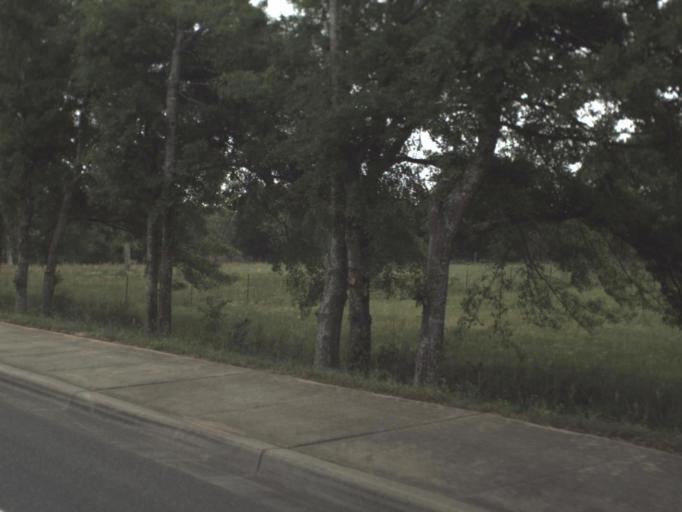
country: US
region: Florida
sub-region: Santa Rosa County
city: Point Baker
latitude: 30.6774
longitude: -87.0542
